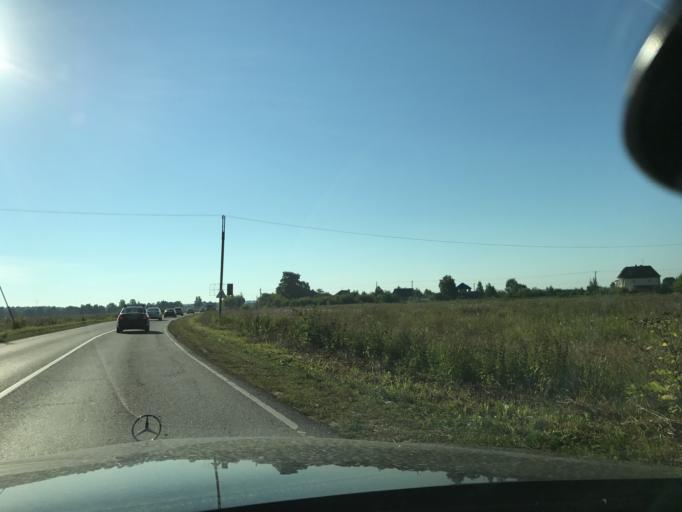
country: RU
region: Moskovskaya
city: Bakhchivandzhi
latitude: 55.8483
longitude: 38.0877
